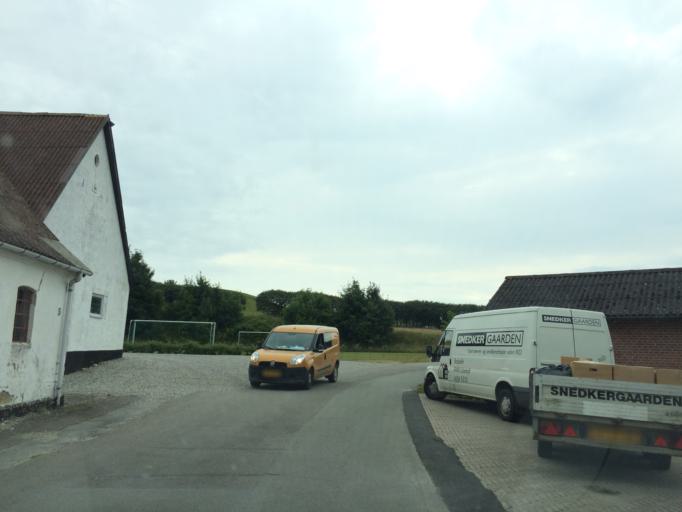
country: DK
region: Central Jutland
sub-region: Syddjurs Kommune
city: Ronde
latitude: 56.2310
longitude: 10.5256
